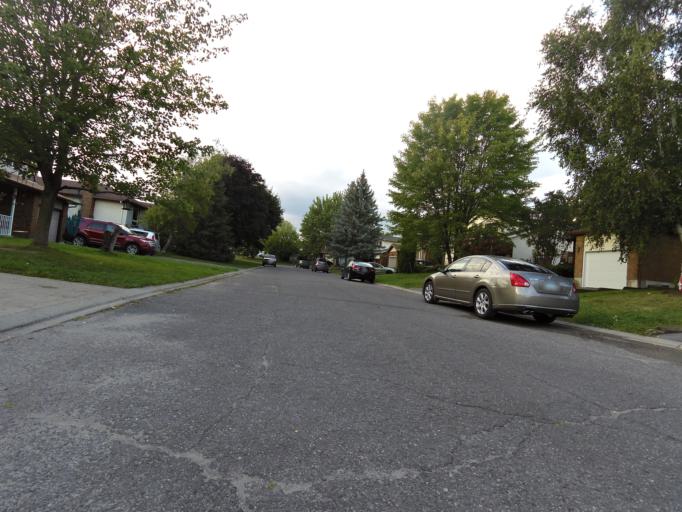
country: CA
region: Ontario
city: Bells Corners
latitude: 45.2756
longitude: -75.7525
